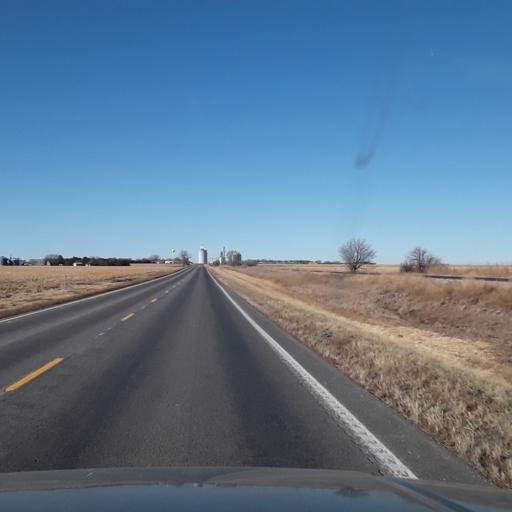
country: US
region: Nebraska
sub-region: Phelps County
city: Holdrege
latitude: 40.4692
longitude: -99.4823
